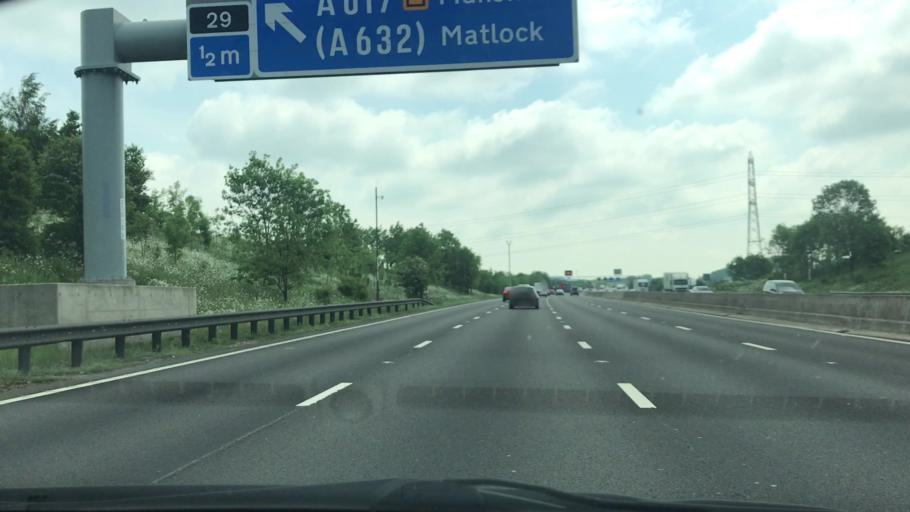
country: GB
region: England
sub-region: Derbyshire
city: Bolsover
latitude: 53.2123
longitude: -1.3233
